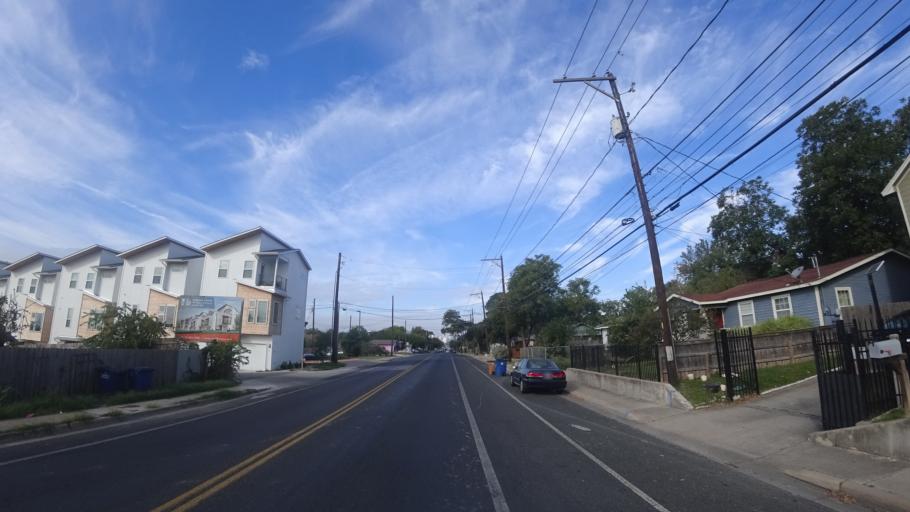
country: US
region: Texas
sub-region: Travis County
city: Austin
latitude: 30.2766
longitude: -97.7025
